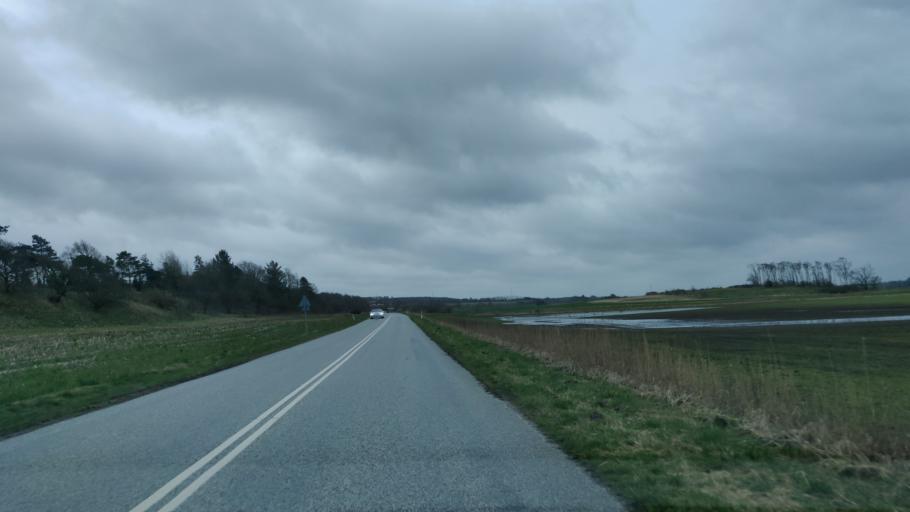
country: DK
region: Central Jutland
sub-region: Skive Kommune
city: Hojslev
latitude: 56.5636
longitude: 9.2496
